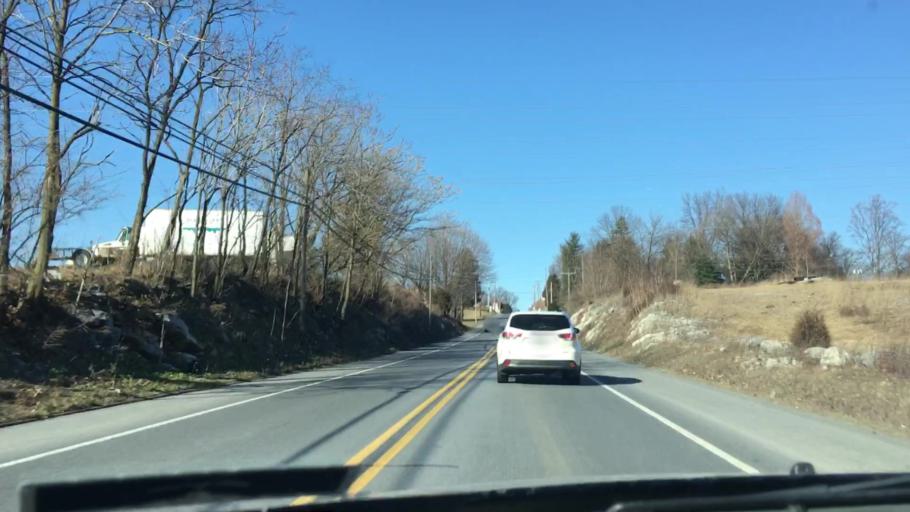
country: US
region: Pennsylvania
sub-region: Lancaster County
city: Akron
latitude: 40.1424
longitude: -76.2104
